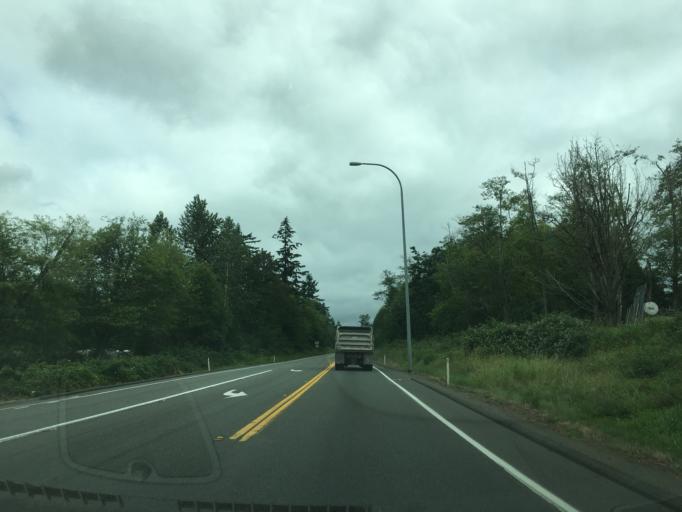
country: US
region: Washington
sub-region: Snohomish County
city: West Lake Stevens
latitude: 48.0342
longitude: -122.1104
